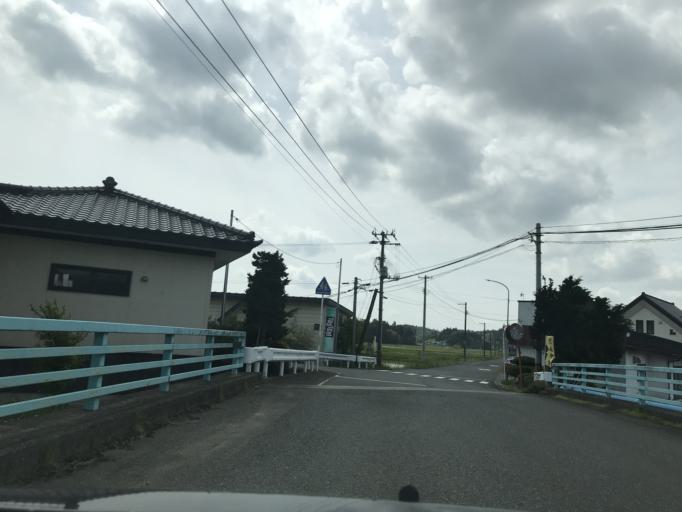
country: JP
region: Iwate
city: Ichinoseki
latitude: 38.8490
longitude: 141.0173
